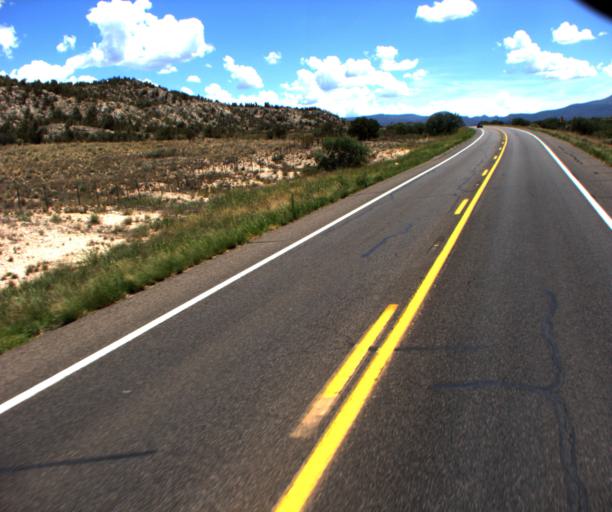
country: US
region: Arizona
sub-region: Yavapai County
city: Camp Verde
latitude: 34.5374
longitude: -111.8192
